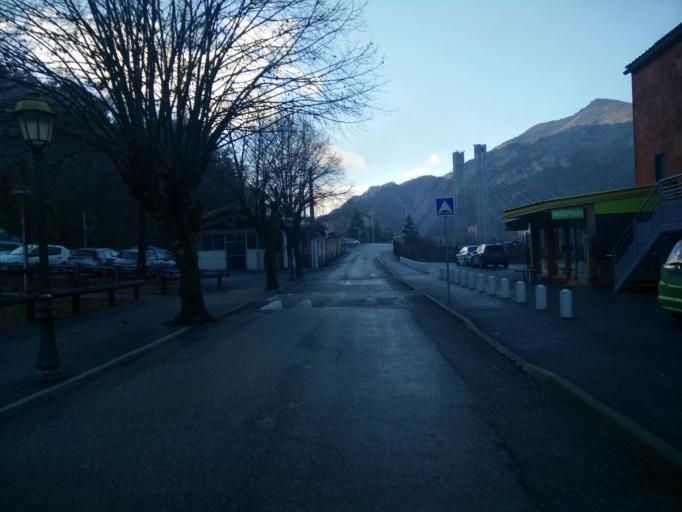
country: FR
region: Provence-Alpes-Cote d'Azur
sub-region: Departement des Alpes-Maritimes
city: Puget-Theniers
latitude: 43.9539
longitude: 6.8976
